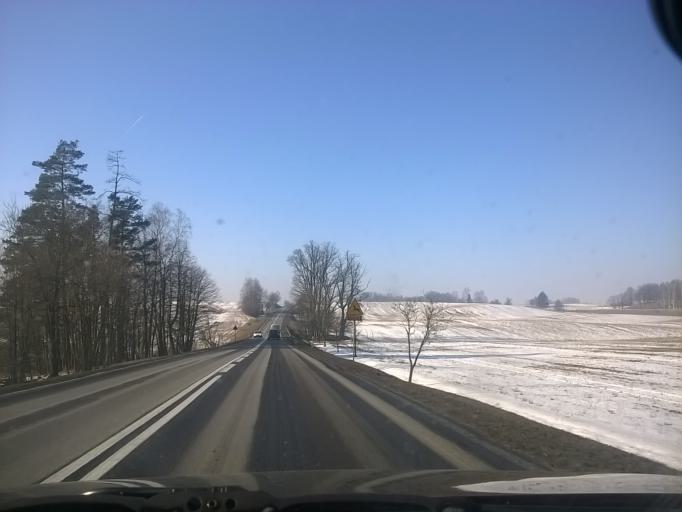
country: PL
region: Warmian-Masurian Voivodeship
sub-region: Powiat mragowski
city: Mragowo
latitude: 53.8400
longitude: 21.1790
